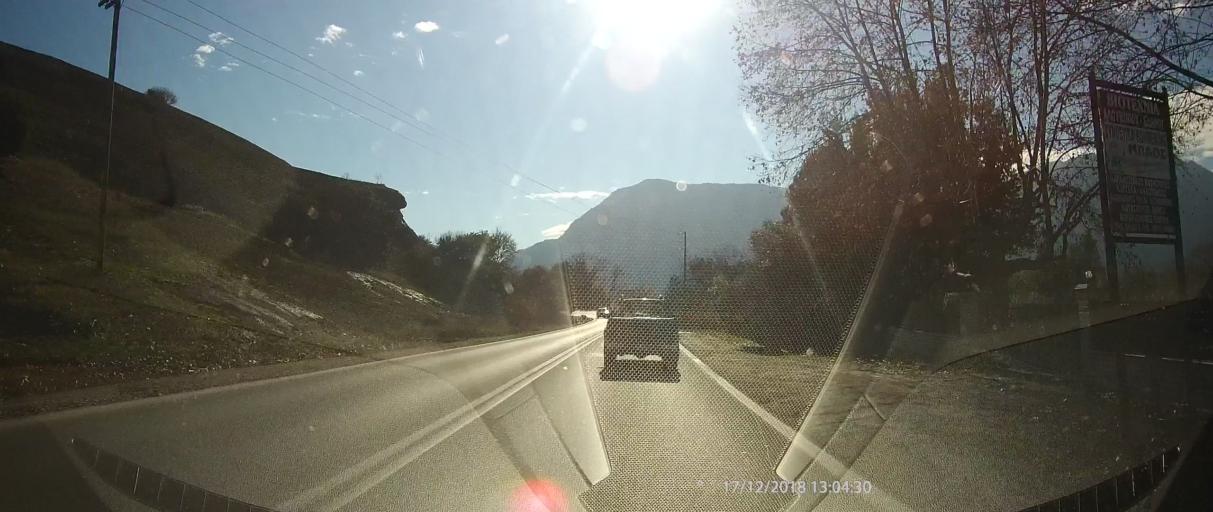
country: GR
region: Thessaly
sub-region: Trikala
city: Kastraki
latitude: 39.7046
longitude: 21.6116
